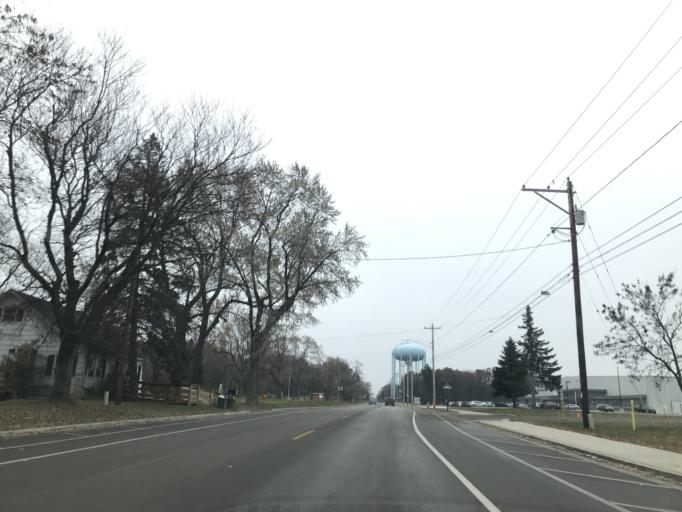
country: US
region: Wisconsin
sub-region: Marinette County
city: Marinette
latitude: 45.0820
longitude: -87.6296
